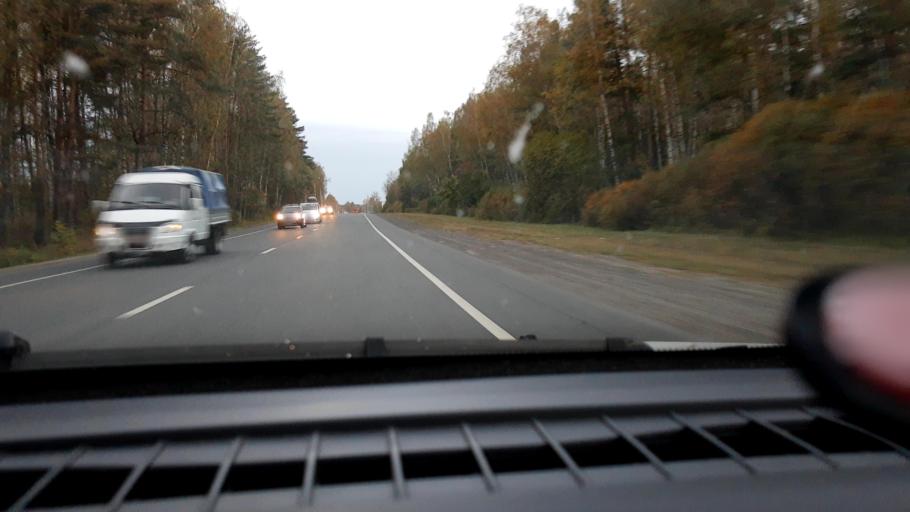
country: RU
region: Vladimir
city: Orgtrud
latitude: 56.2071
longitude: 40.6911
